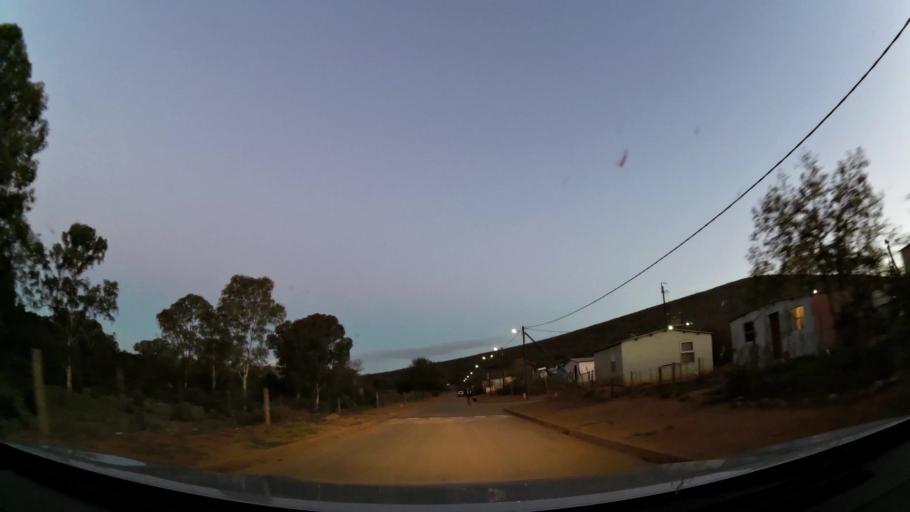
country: ZA
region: Western Cape
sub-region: Eden District Municipality
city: Riversdale
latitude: -34.1059
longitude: 21.2750
